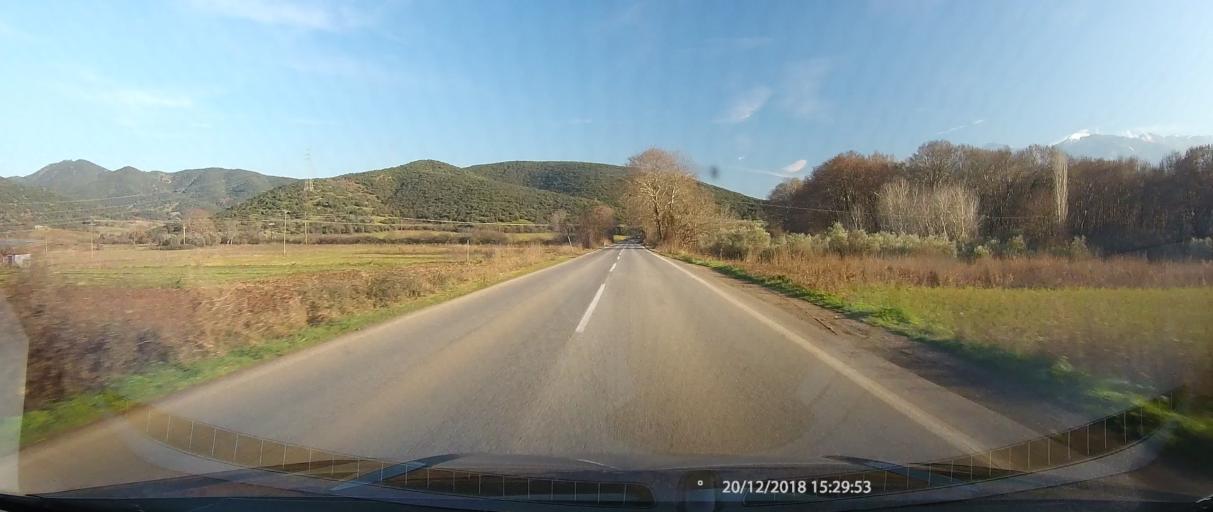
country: GR
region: Central Greece
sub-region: Nomos Fthiotidos
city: Lianokladhion
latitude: 38.9420
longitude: 22.2172
